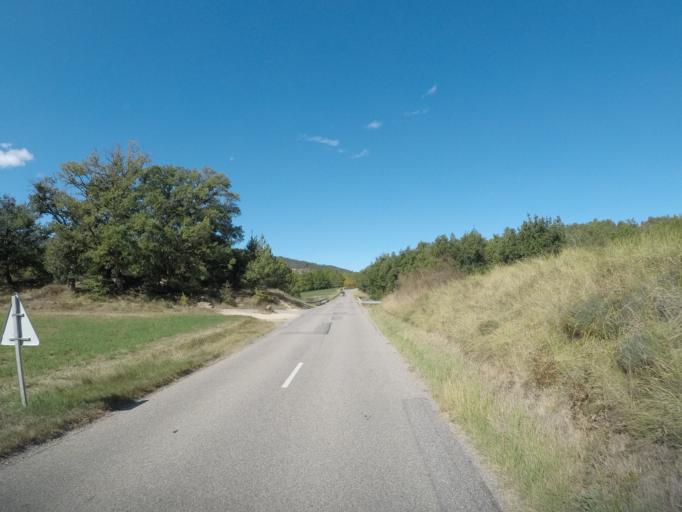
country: FR
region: Provence-Alpes-Cote d'Azur
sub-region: Departement des Alpes-de-Haute-Provence
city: Mallemoisson
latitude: 44.0121
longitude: 6.1869
